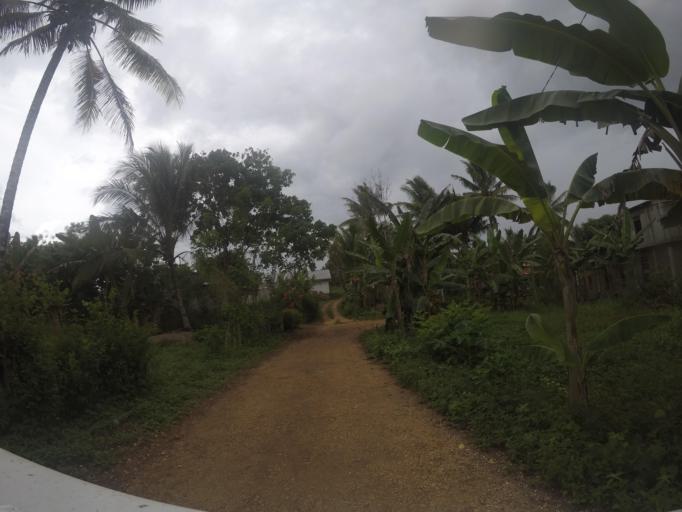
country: TL
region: Lautem
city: Lospalos
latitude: -8.5292
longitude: 126.9938
